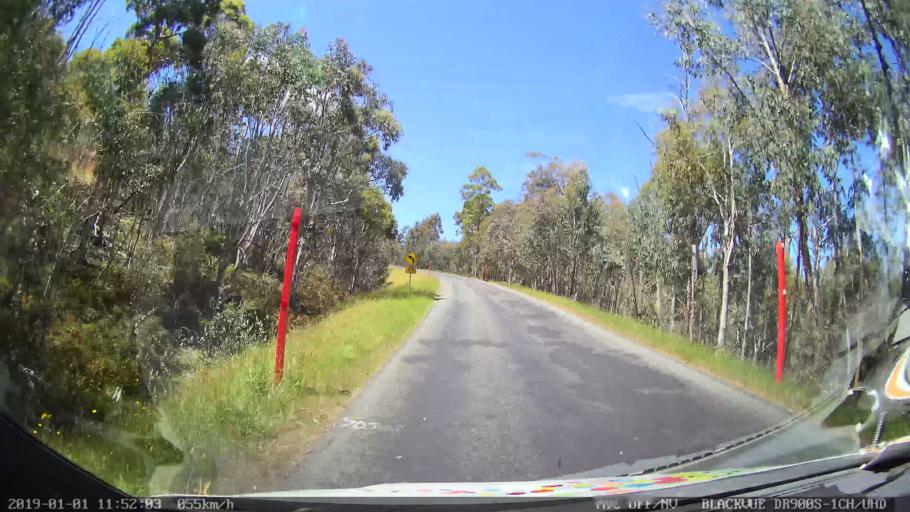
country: AU
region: New South Wales
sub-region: Snowy River
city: Jindabyne
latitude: -35.8870
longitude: 148.4327
